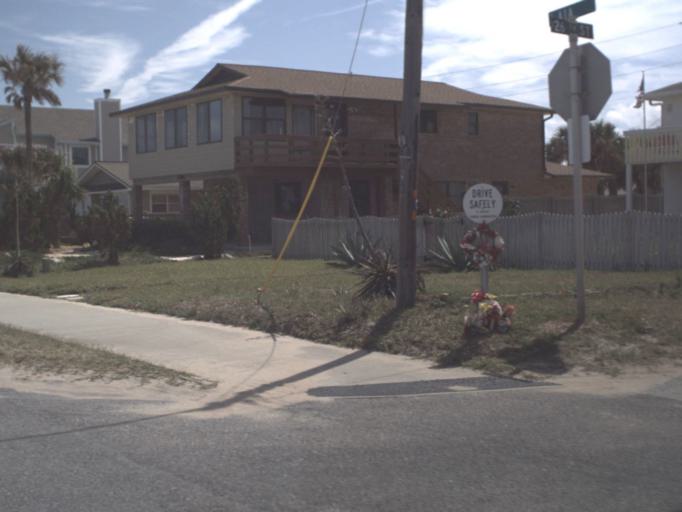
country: US
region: Florida
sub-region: Flagler County
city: Flagler Beach
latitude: 29.4479
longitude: -81.1120
